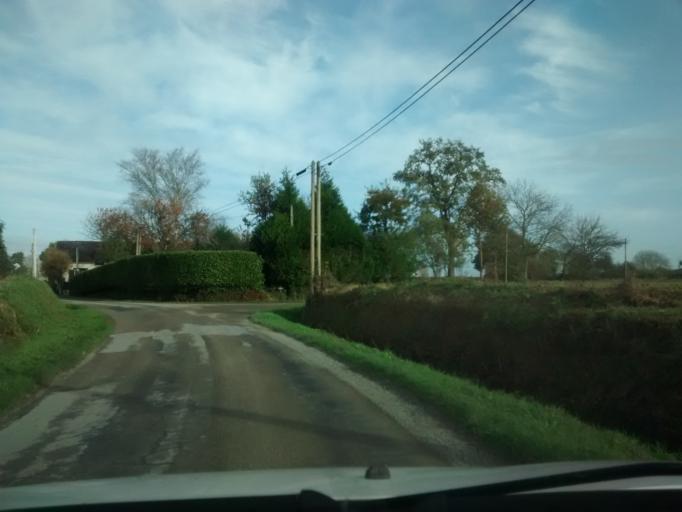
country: FR
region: Brittany
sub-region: Departement d'Ille-et-Vilaine
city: Servon-sur-Vilaine
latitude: 48.1401
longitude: -1.4729
